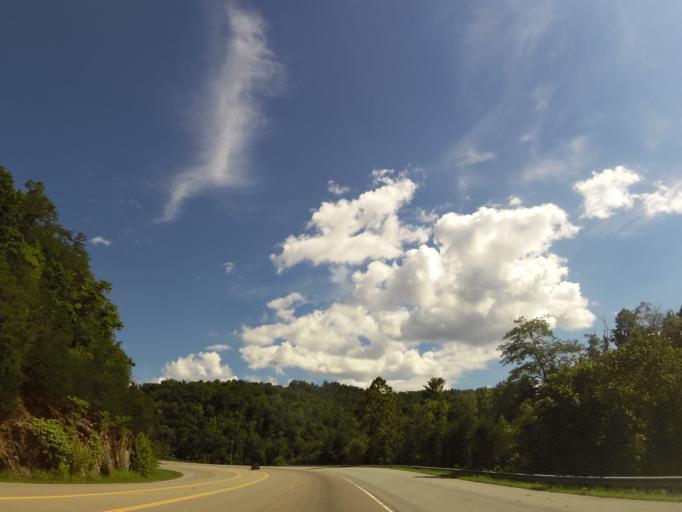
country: US
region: Tennessee
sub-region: Grainger County
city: Rutledge
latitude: 36.3788
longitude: -83.4467
